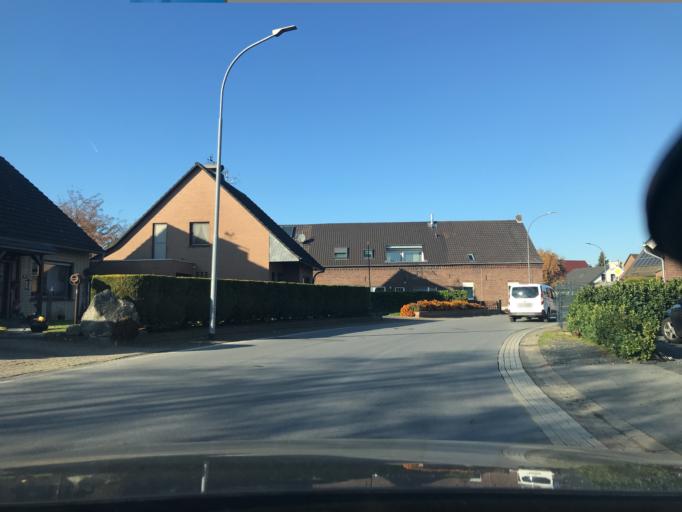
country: DE
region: North Rhine-Westphalia
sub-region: Regierungsbezirk Dusseldorf
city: Wachtendonk
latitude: 51.4349
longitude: 6.4011
